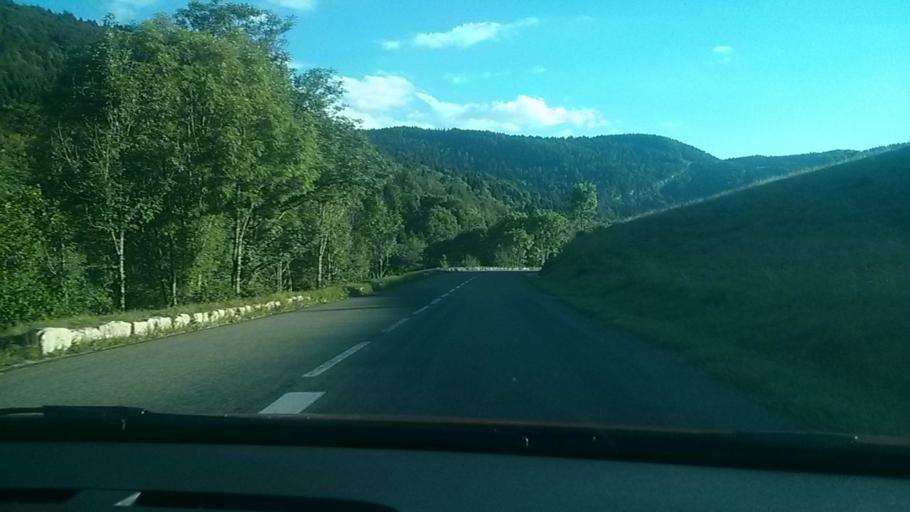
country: FR
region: Franche-Comte
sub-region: Departement du Jura
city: Saint-Claude
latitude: 46.3664
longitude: 5.9139
